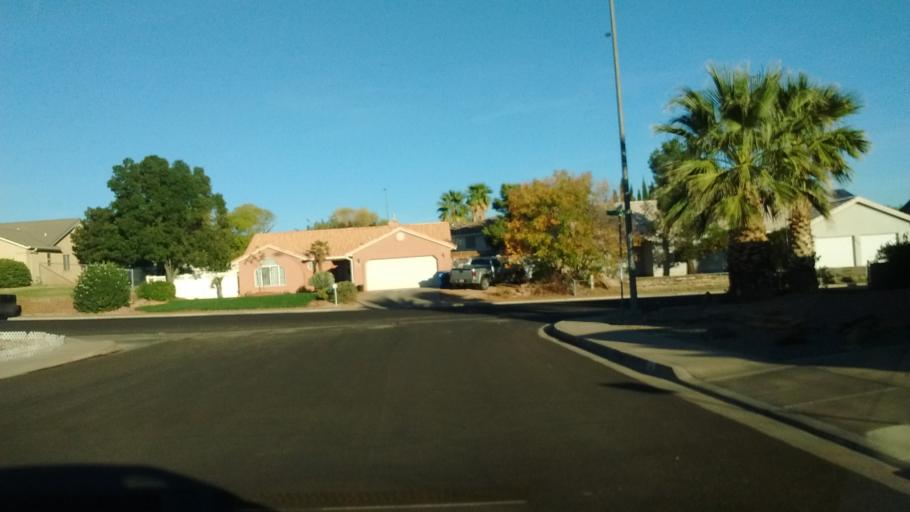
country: US
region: Utah
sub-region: Washington County
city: Washington
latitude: 37.1384
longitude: -113.4981
